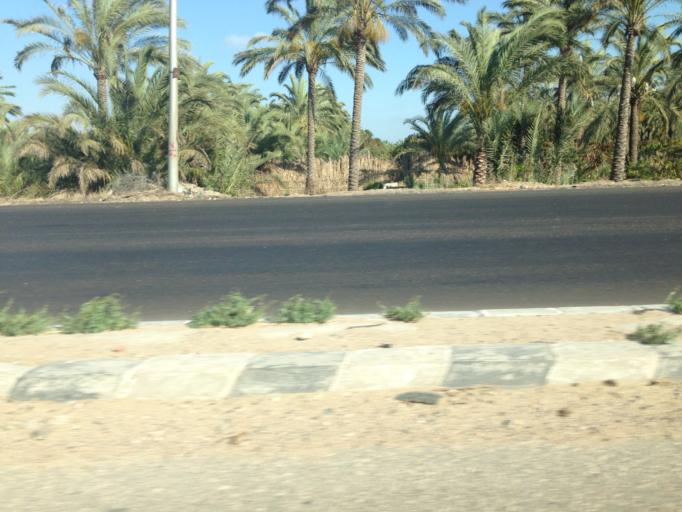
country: EG
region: Al Buhayrah
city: Idku
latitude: 31.3035
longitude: 30.2708
